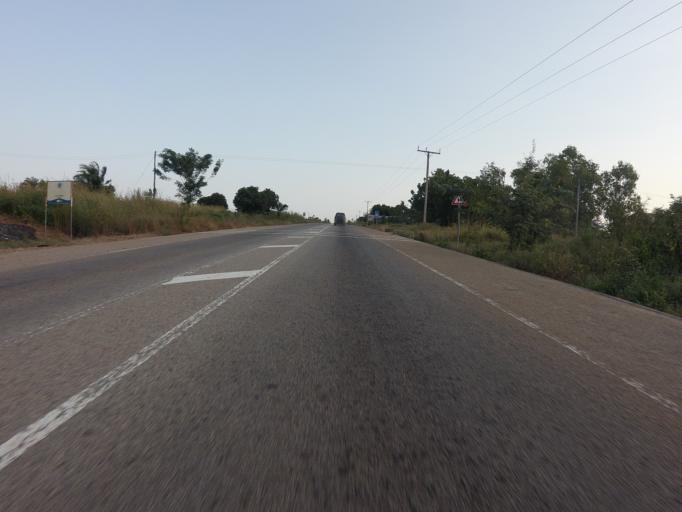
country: GH
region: Volta
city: Anloga
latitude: 6.0399
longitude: 0.6047
